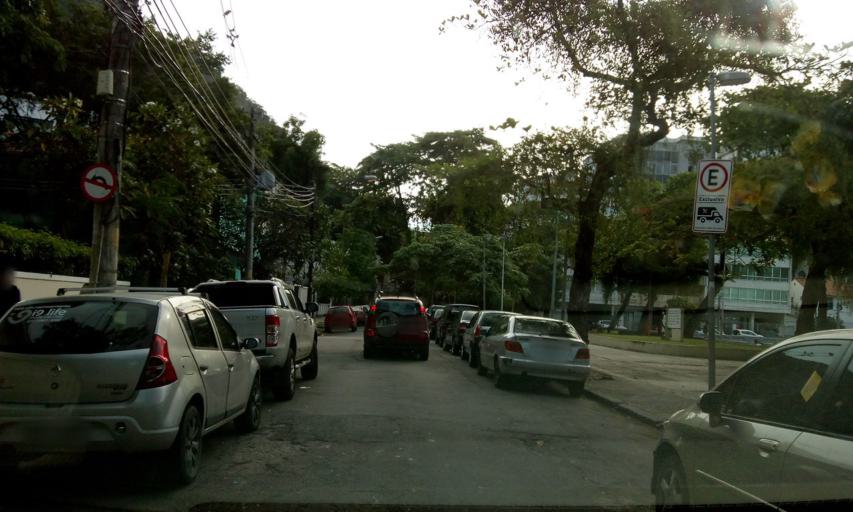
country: BR
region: Rio de Janeiro
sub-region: Rio De Janeiro
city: Rio de Janeiro
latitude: -22.9527
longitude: -43.1689
